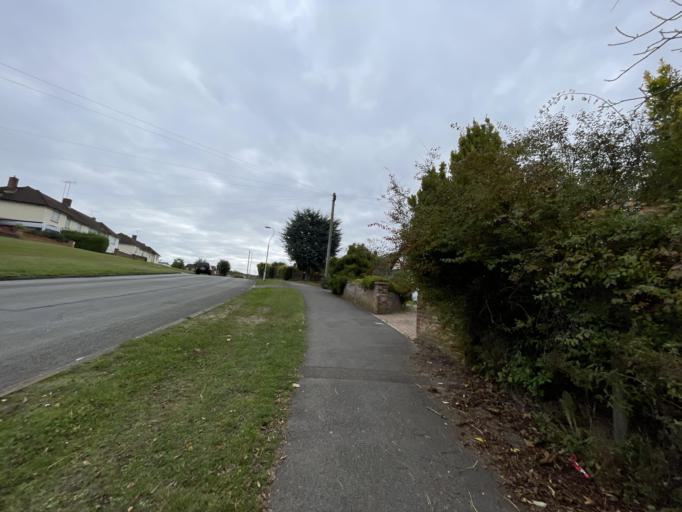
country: GB
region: England
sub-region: West Berkshire
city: Tilehurst
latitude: 51.4582
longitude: -1.0272
